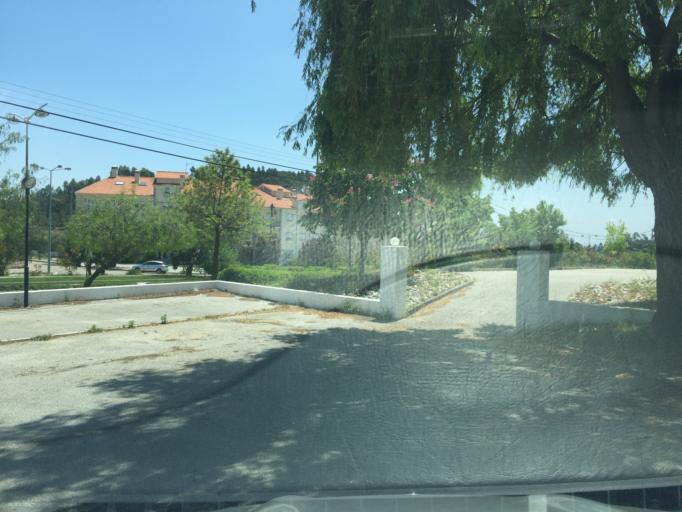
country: PT
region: Castelo Branco
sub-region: Vila de Rei
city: Vila de Rei
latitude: 39.6761
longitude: -8.1429
